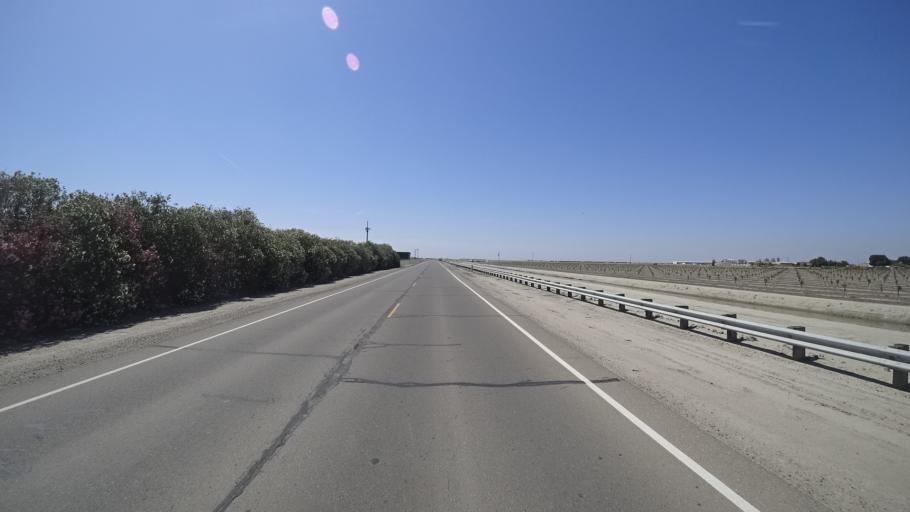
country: US
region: California
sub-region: Kings County
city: Corcoran
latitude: 36.0755
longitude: -119.5586
